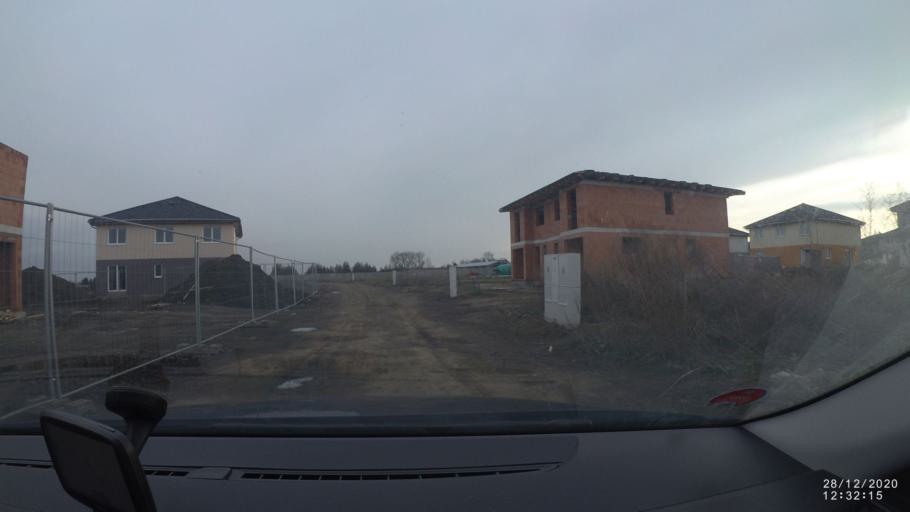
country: CZ
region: Central Bohemia
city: Kostelec nad Labem
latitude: 50.2031
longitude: 14.5927
